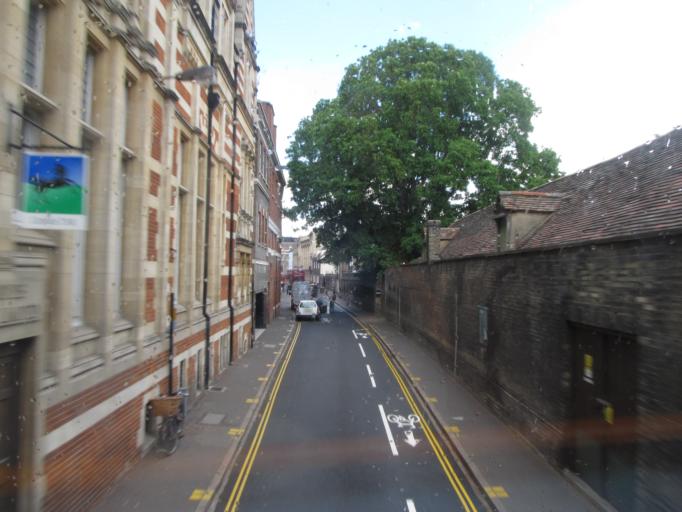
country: GB
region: England
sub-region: Cambridgeshire
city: Cambridge
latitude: 52.2054
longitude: 0.1217
